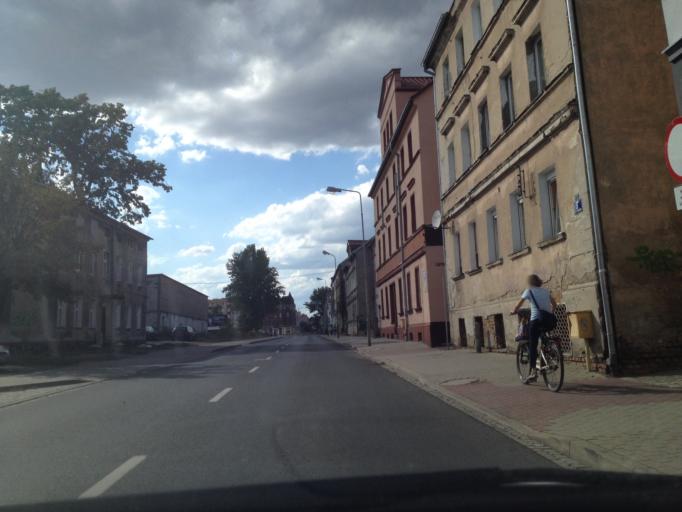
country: PL
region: Lubusz
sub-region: Powiat zarski
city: Zary
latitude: 51.6394
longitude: 15.1309
